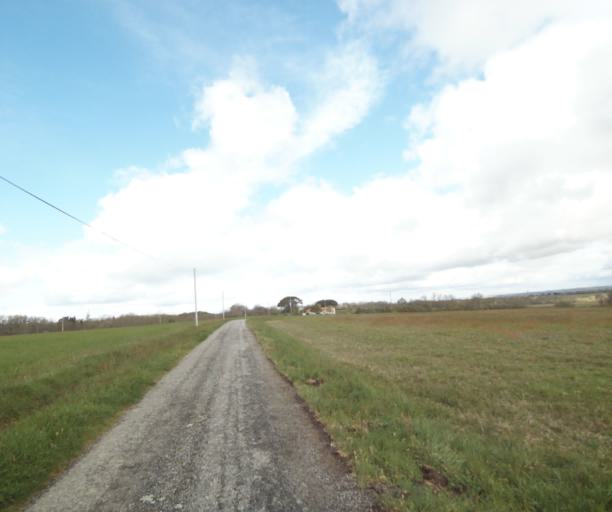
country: FR
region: Midi-Pyrenees
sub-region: Departement de l'Ariege
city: Saverdun
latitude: 43.2306
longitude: 1.5351
